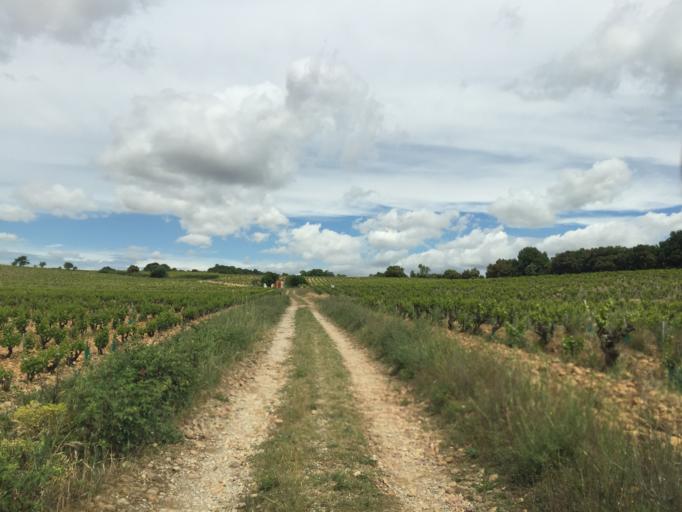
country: FR
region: Provence-Alpes-Cote d'Azur
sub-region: Departement du Vaucluse
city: Bedarrides
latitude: 44.0384
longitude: 4.8758
